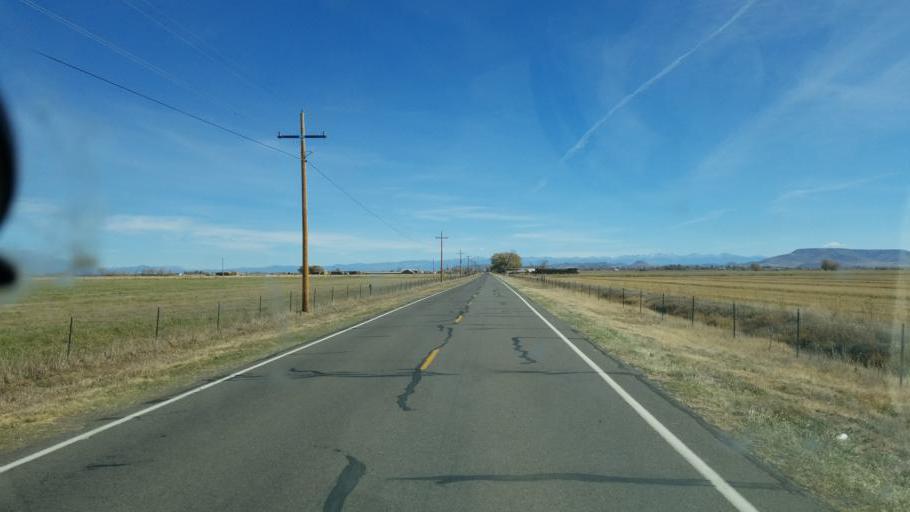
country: US
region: Colorado
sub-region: Conejos County
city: Conejos
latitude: 37.2835
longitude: -106.0052
